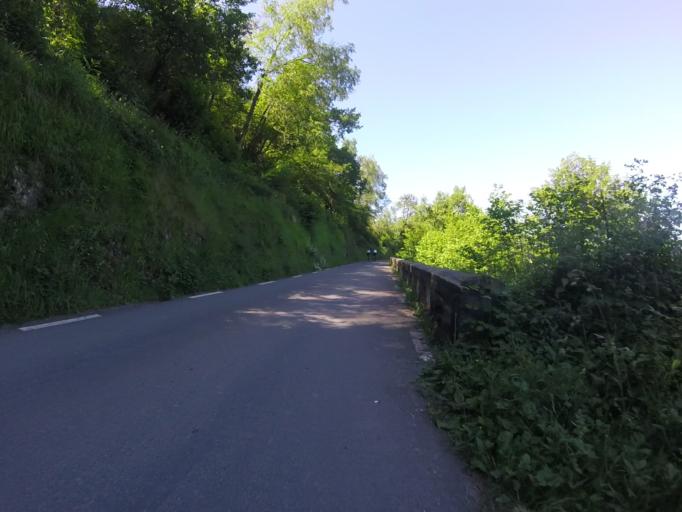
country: ES
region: Basque Country
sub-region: Provincia de Guipuzcoa
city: Beizama
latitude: 43.1314
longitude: -2.1949
